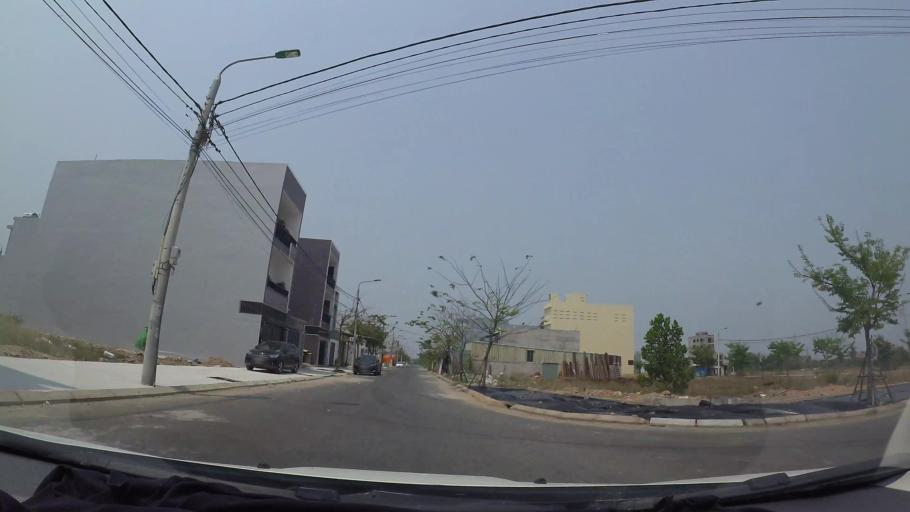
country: VN
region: Da Nang
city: Cam Le
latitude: 16.0160
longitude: 108.2220
